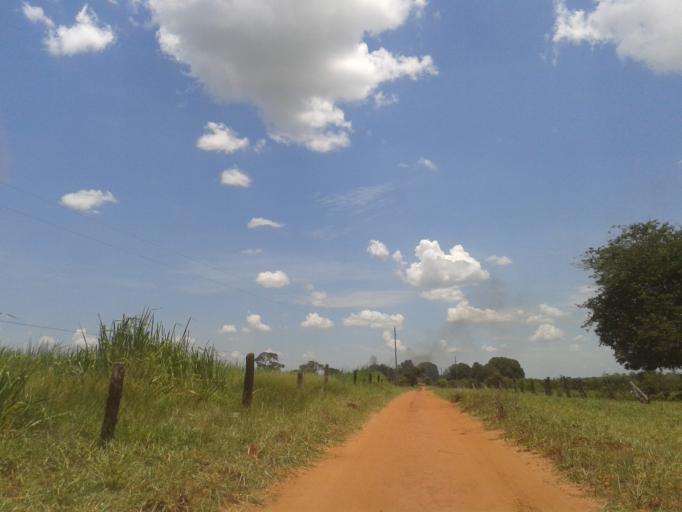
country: BR
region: Minas Gerais
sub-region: Santa Vitoria
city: Santa Vitoria
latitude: -19.2260
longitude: -50.4600
